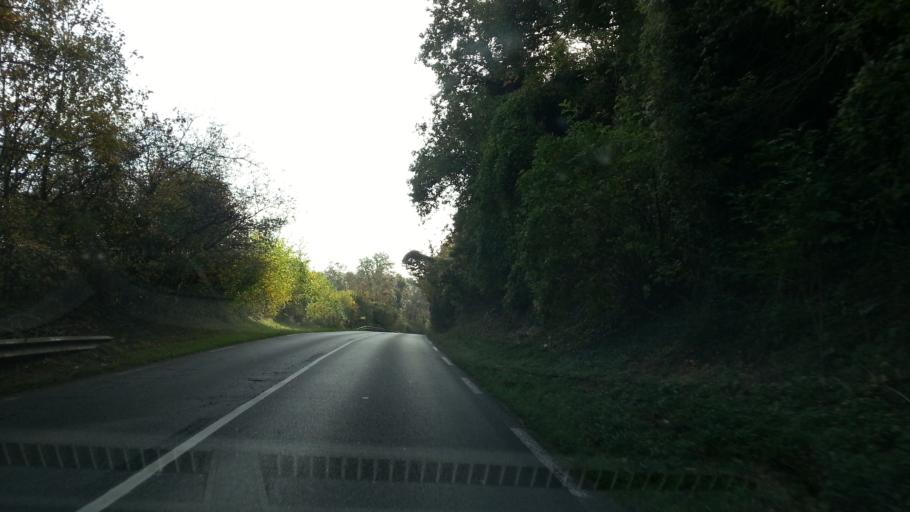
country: FR
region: Picardie
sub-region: Departement de l'Oise
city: Precy-sur-Oise
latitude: 49.1948
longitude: 2.3650
